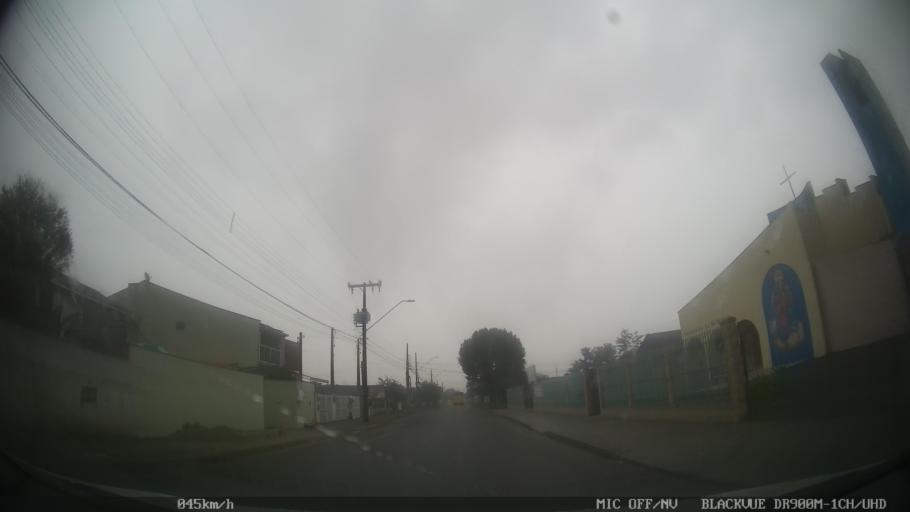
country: BR
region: Santa Catarina
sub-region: Joinville
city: Joinville
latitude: -26.2080
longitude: -48.8307
